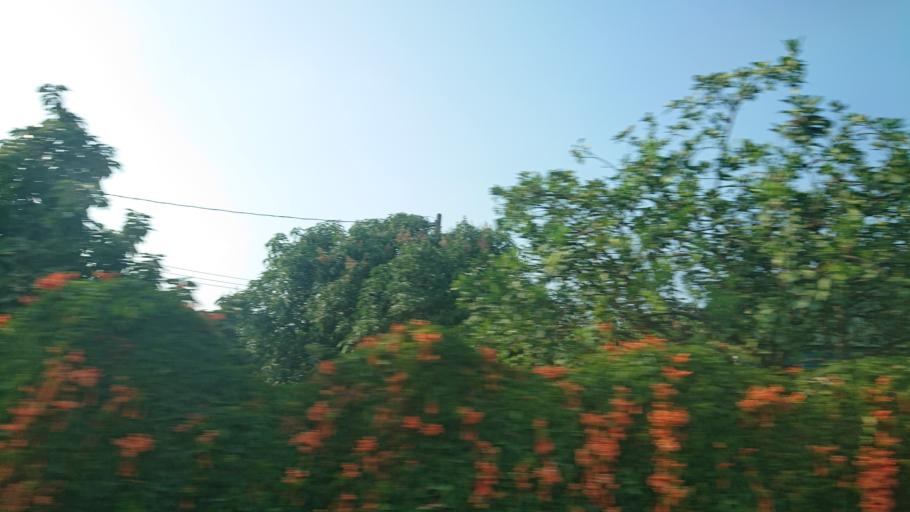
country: TW
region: Taiwan
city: Xinying
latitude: 23.1787
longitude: 120.2630
